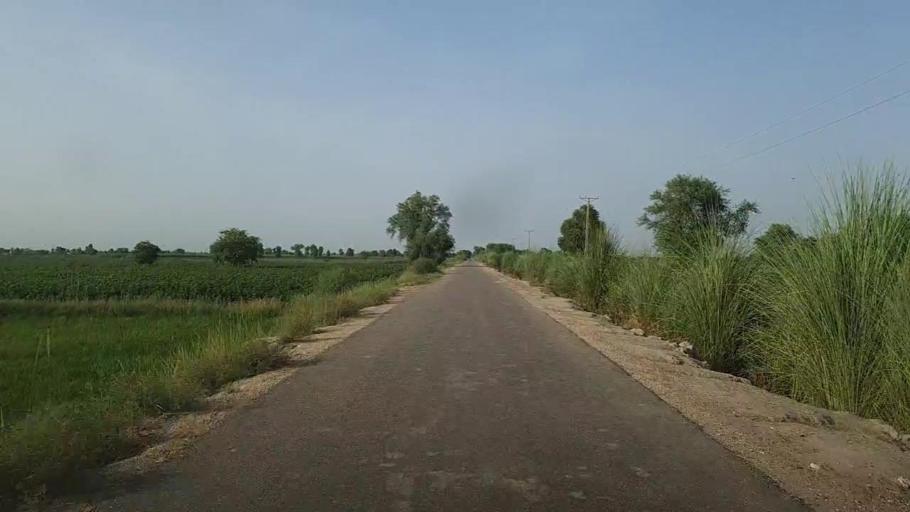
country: PK
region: Sindh
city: Ubauro
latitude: 28.0906
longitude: 69.8192
